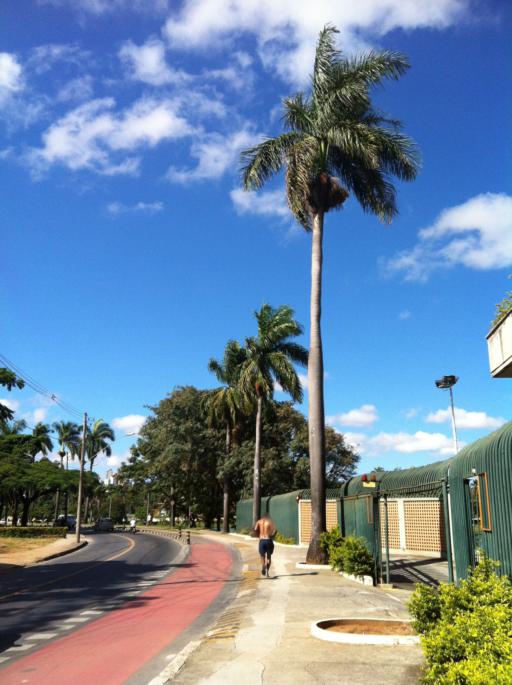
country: BR
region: Minas Gerais
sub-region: Belo Horizonte
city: Belo Horizonte
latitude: -19.8562
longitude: -43.9770
